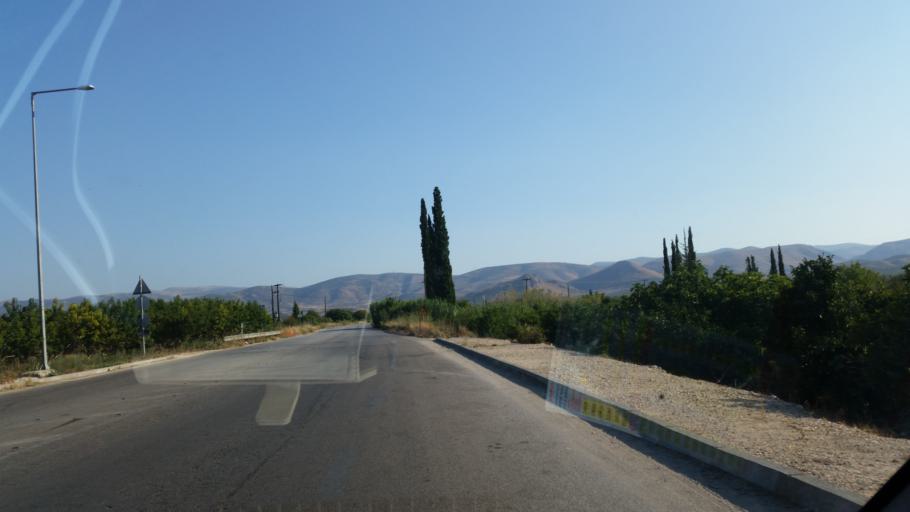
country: GR
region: Peloponnese
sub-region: Nomos Argolidos
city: Nea Tirins
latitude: 37.6156
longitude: 22.8129
